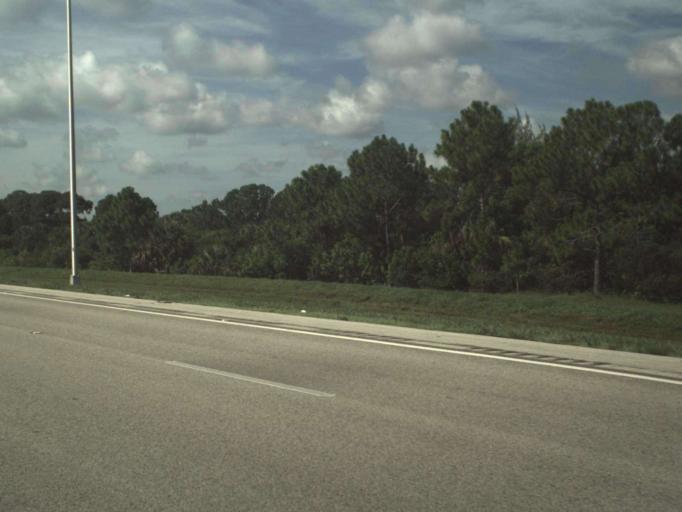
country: US
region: Florida
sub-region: Palm Beach County
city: Limestone Creek
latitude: 26.9252
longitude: -80.1479
